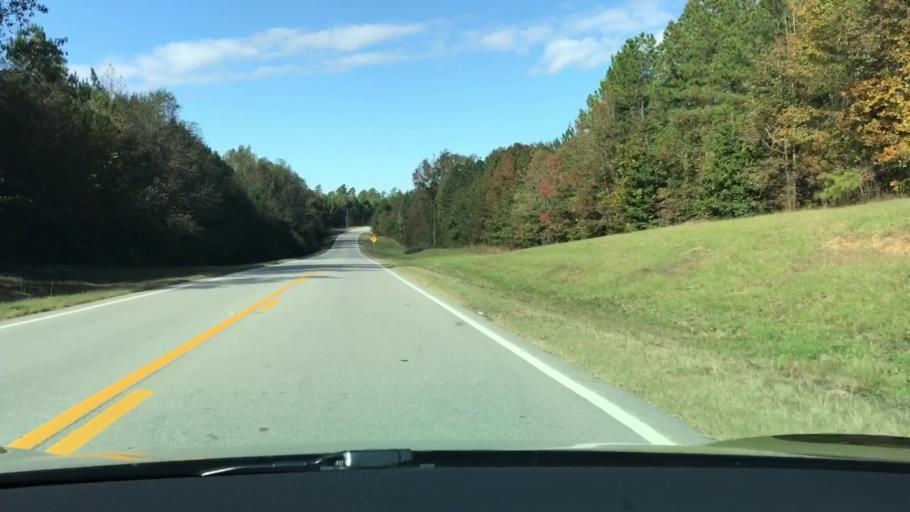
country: US
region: Georgia
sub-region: Jefferson County
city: Wrens
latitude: 33.2638
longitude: -82.4854
